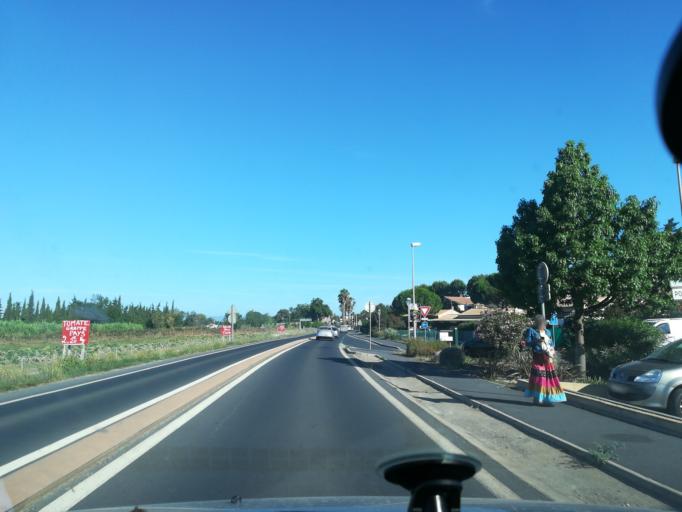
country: FR
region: Languedoc-Roussillon
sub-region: Departement de l'Herault
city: Portiragnes
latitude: 43.3022
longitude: 3.3330
